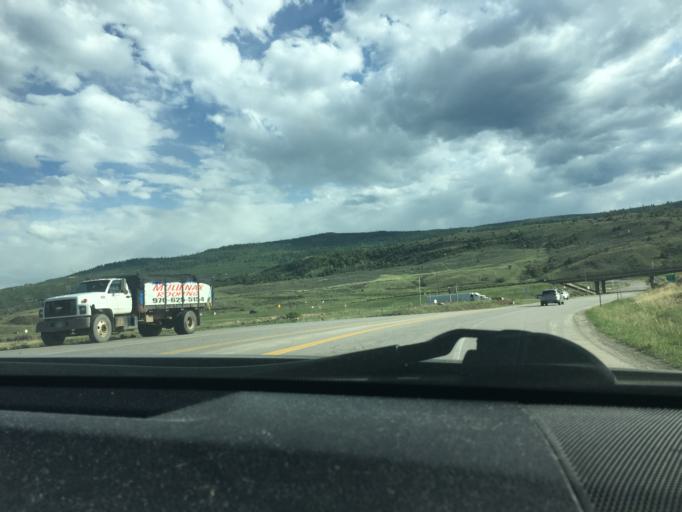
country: US
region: Colorado
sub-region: Eagle County
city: Edwards
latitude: 39.6992
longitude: -106.6701
